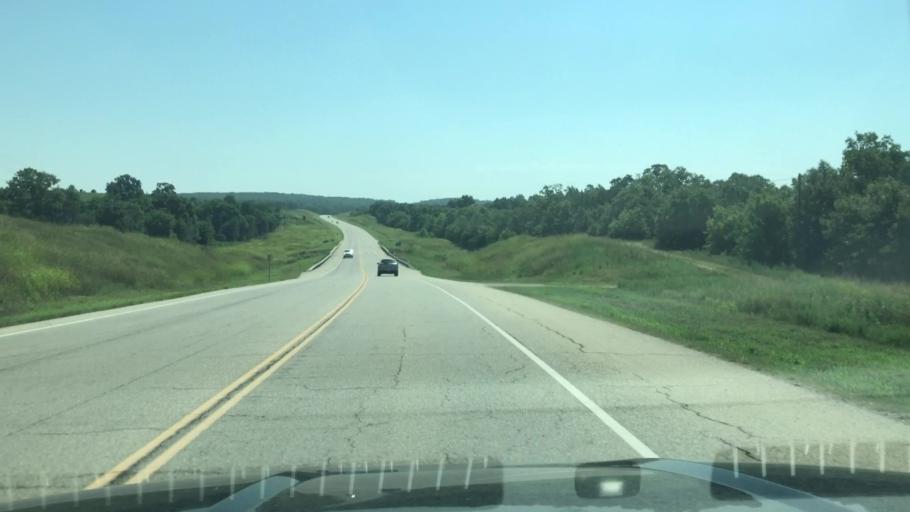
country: US
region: Oklahoma
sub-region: Creek County
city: Kellyville
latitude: 35.9867
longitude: -96.3274
